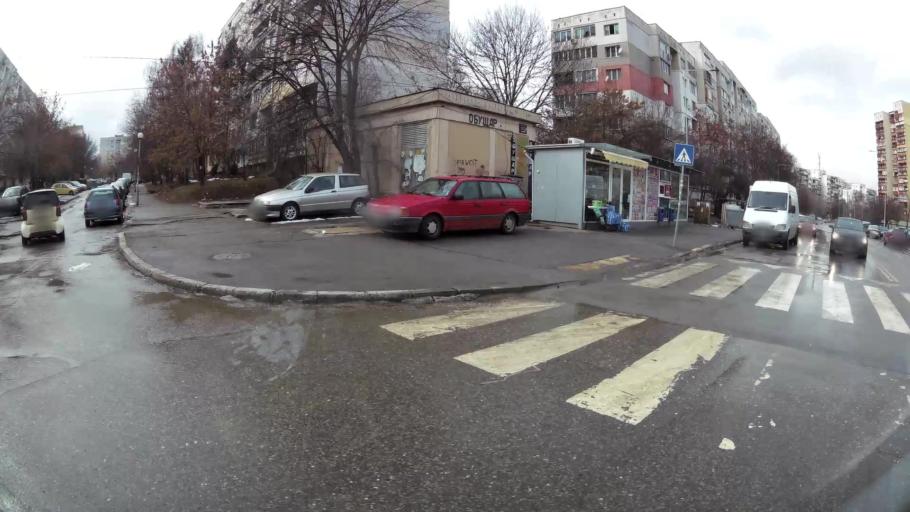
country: BG
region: Sofiya
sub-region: Obshtina Bozhurishte
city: Bozhurishte
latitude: 42.7144
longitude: 23.2450
